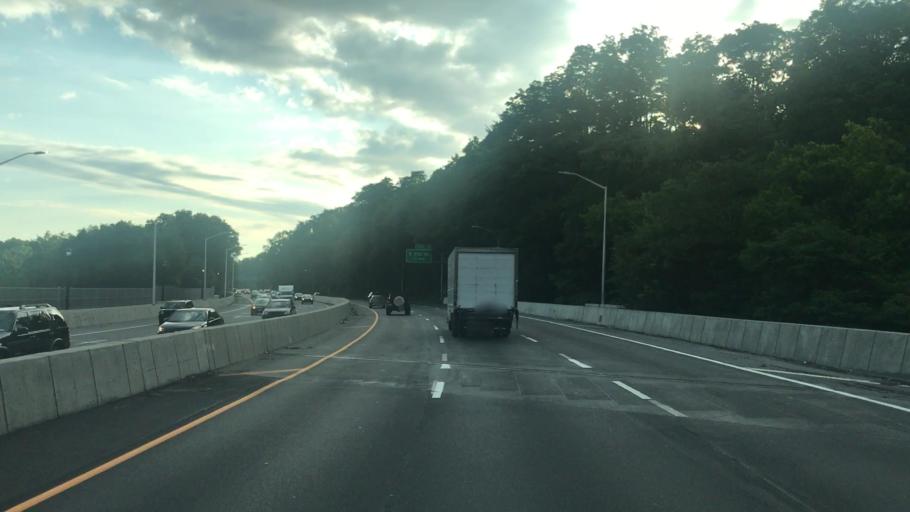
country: US
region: New York
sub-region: Westchester County
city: Yonkers
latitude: 40.8895
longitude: -73.8880
